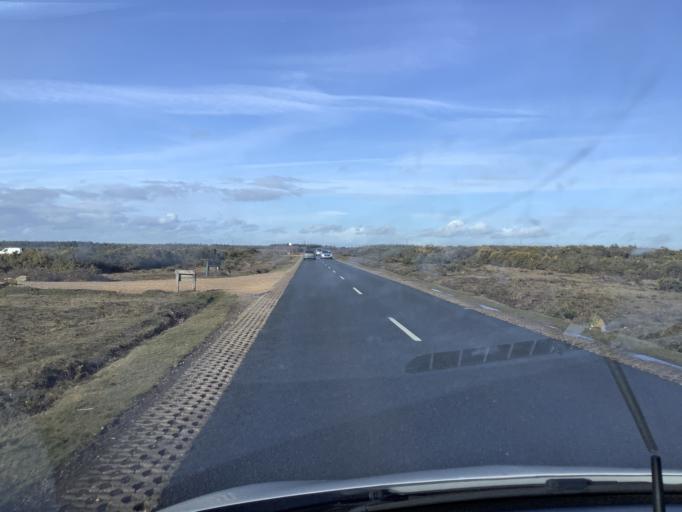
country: GB
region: England
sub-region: Hampshire
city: Hythe
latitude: 50.8313
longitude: -1.4302
